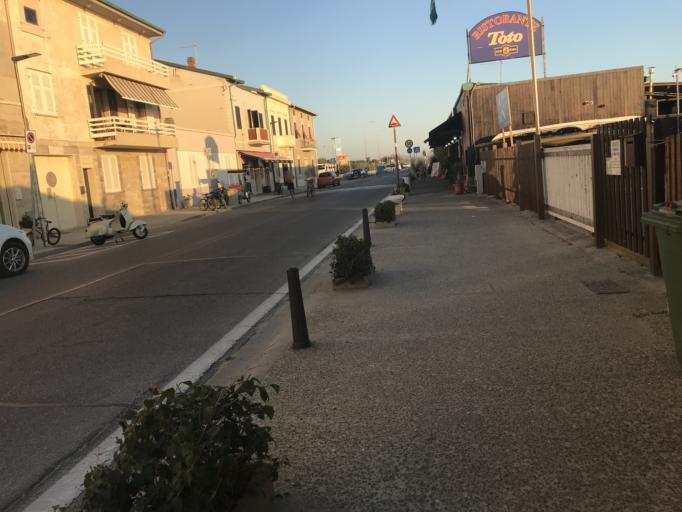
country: IT
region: Tuscany
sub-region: Province of Pisa
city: Marina di Pisa
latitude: 43.6598
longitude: 10.2796
